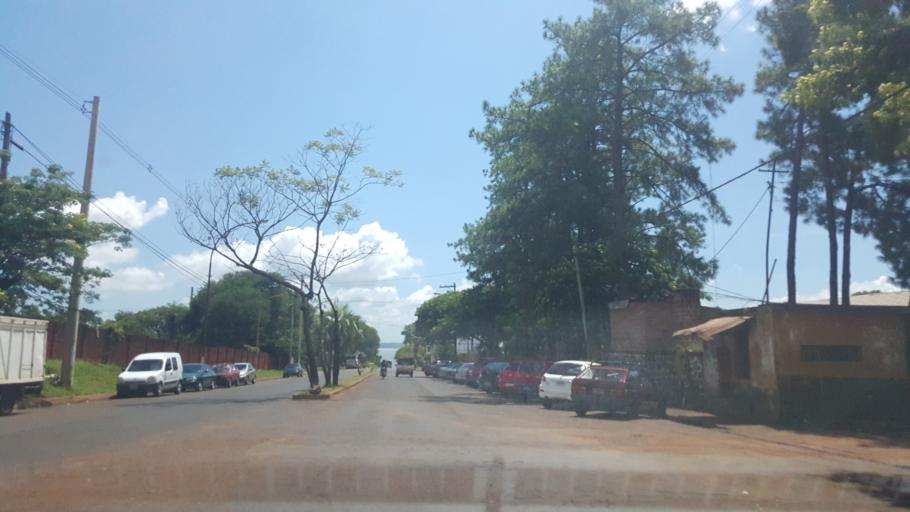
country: AR
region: Misiones
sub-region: Departamento de Capital
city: Posadas
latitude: -27.3600
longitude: -55.9156
